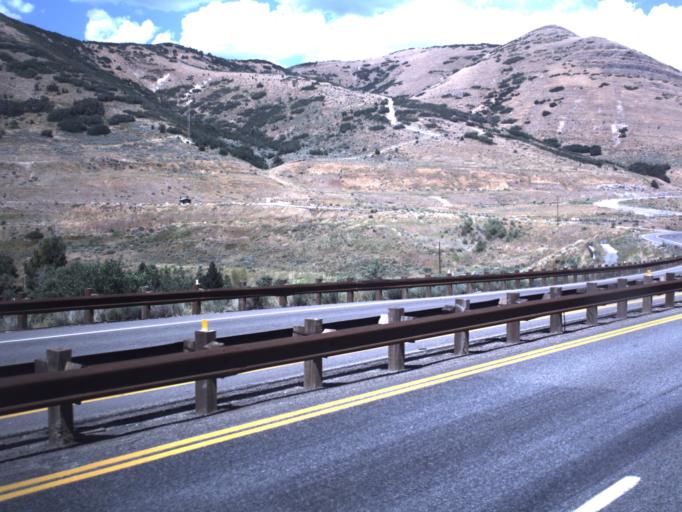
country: US
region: Utah
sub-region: Wasatch County
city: Midway
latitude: 40.4024
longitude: -111.5333
